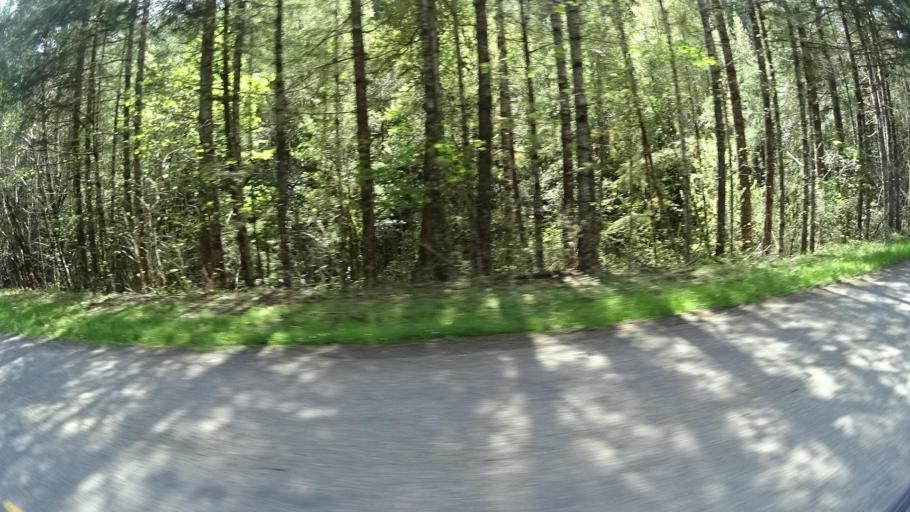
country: US
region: California
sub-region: Humboldt County
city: Redway
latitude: 40.4398
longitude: -123.7852
